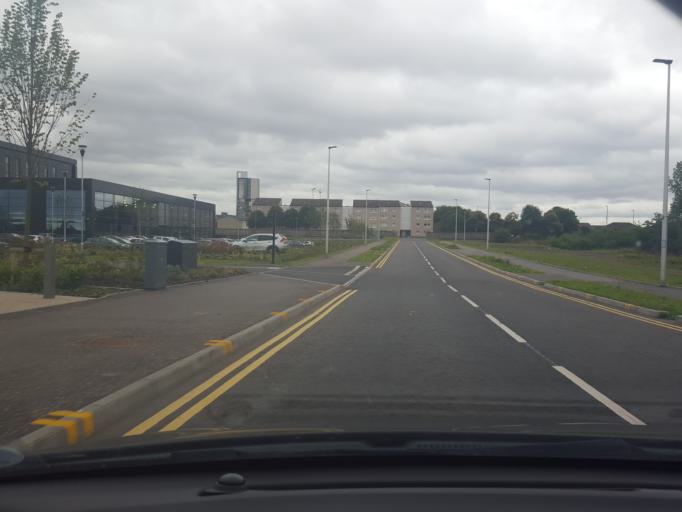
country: GB
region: Scotland
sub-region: Glasgow City
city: Glasgow
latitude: 55.8558
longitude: -4.2914
